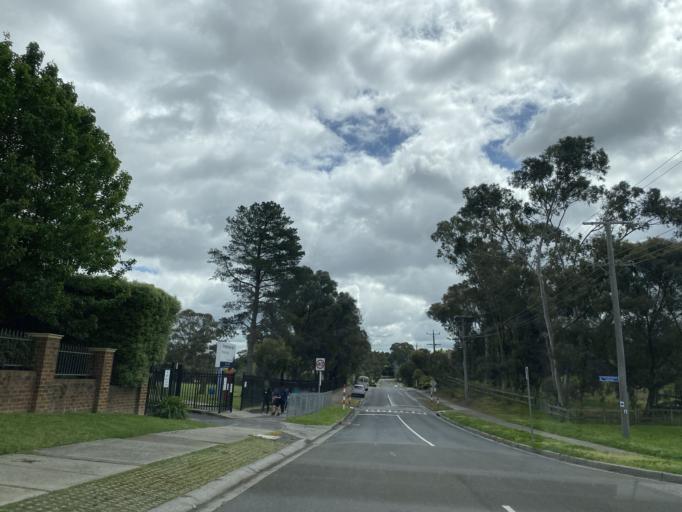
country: AU
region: Victoria
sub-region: Nillumbik
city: Eltham
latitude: -37.7566
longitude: 145.1434
